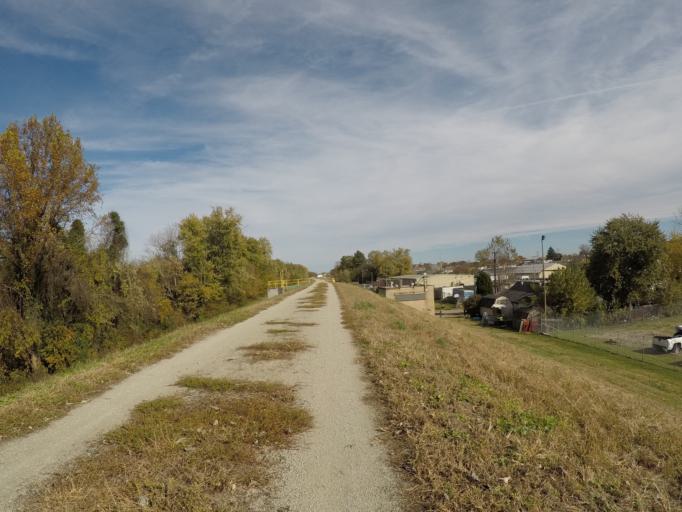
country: US
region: West Virginia
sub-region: Cabell County
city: Huntington
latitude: 38.4180
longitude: -82.4689
